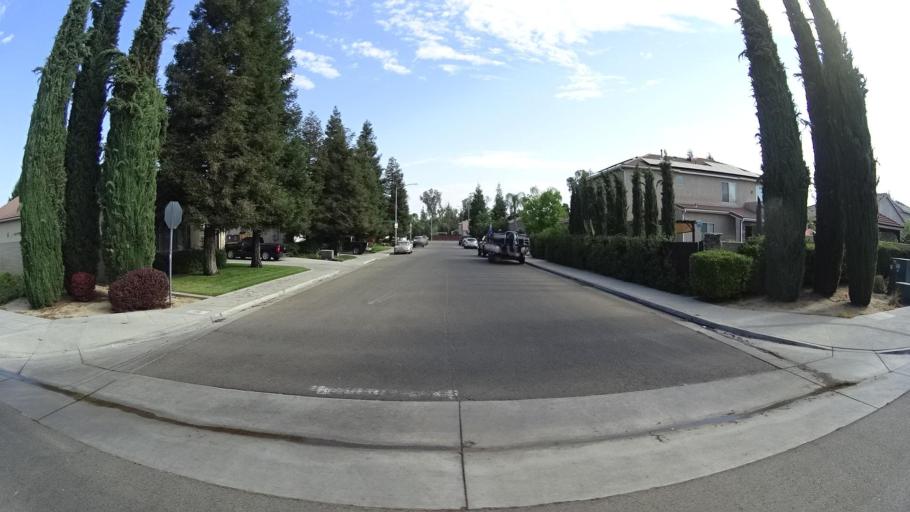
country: US
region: California
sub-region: Fresno County
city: Sunnyside
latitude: 36.7200
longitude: -119.6932
